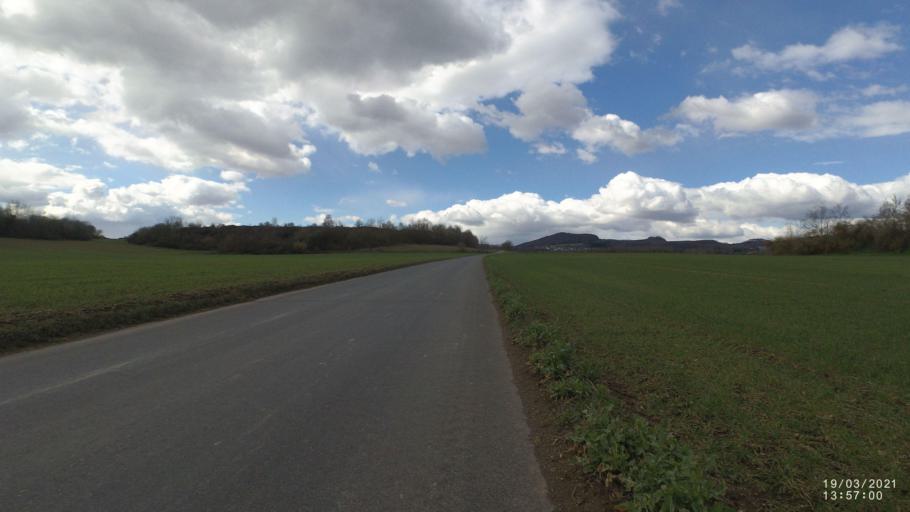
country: DE
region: Rheinland-Pfalz
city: Kretz
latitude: 50.4038
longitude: 7.3474
